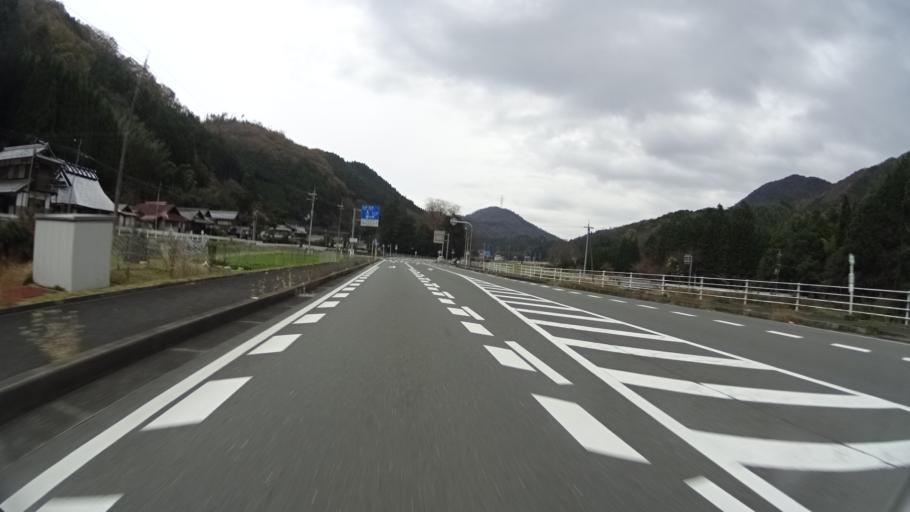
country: JP
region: Hyogo
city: Sasayama
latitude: 35.0671
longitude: 135.3965
